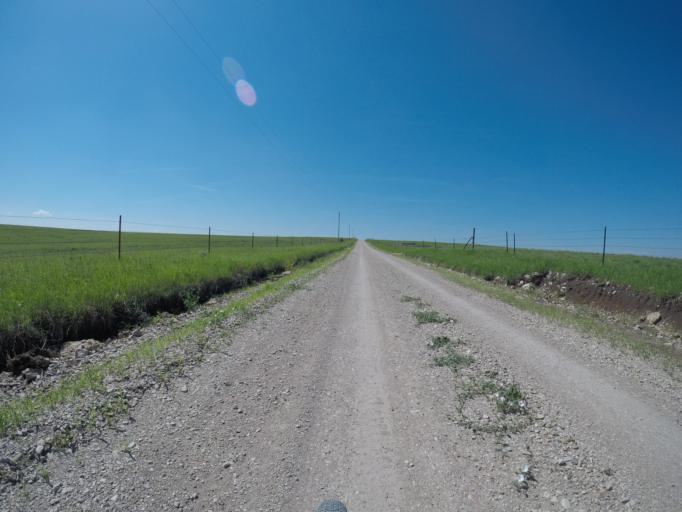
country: US
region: Kansas
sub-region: Wabaunsee County
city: Alma
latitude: 39.0125
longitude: -96.1784
